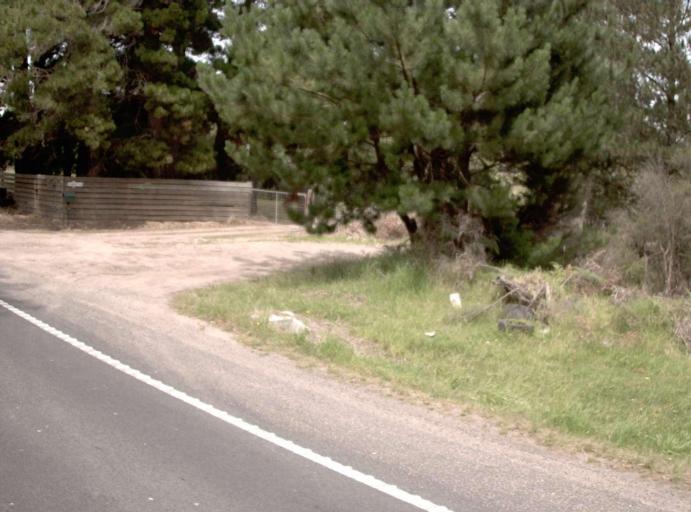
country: AU
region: Victoria
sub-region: Mornington Peninsula
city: Tyabb
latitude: -38.2482
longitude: 145.2150
